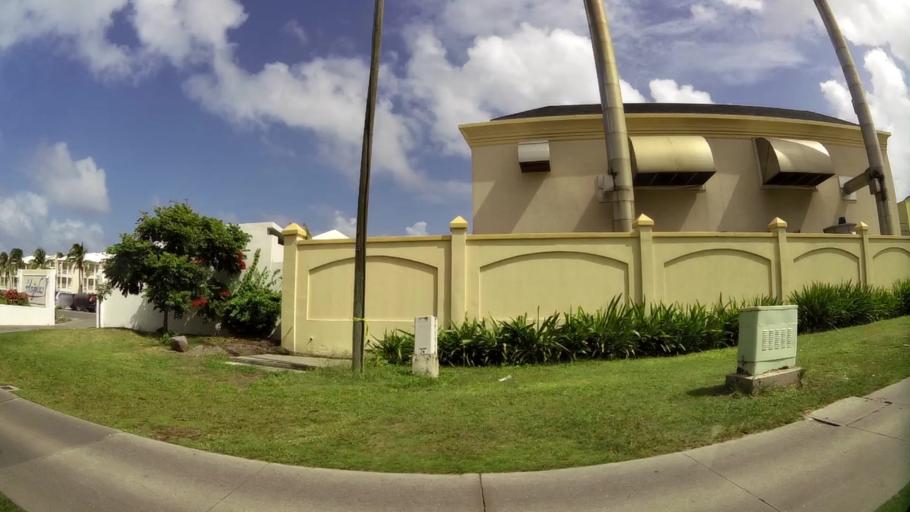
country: KN
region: Saint Peter Basseterre
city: Monkey Hill
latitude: 17.2939
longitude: -62.6862
